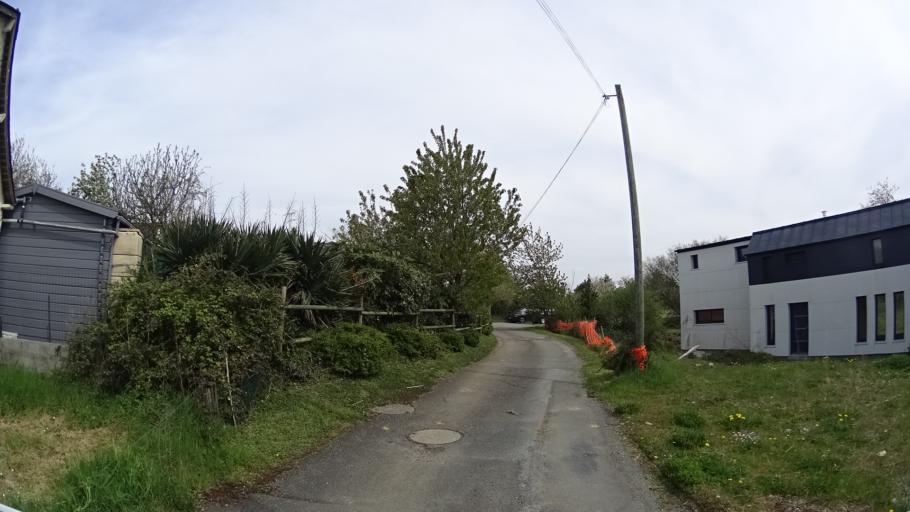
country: FR
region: Brittany
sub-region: Departement d'Ille-et-Vilaine
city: Chartres-de-Bretagne
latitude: 48.0321
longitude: -1.7178
